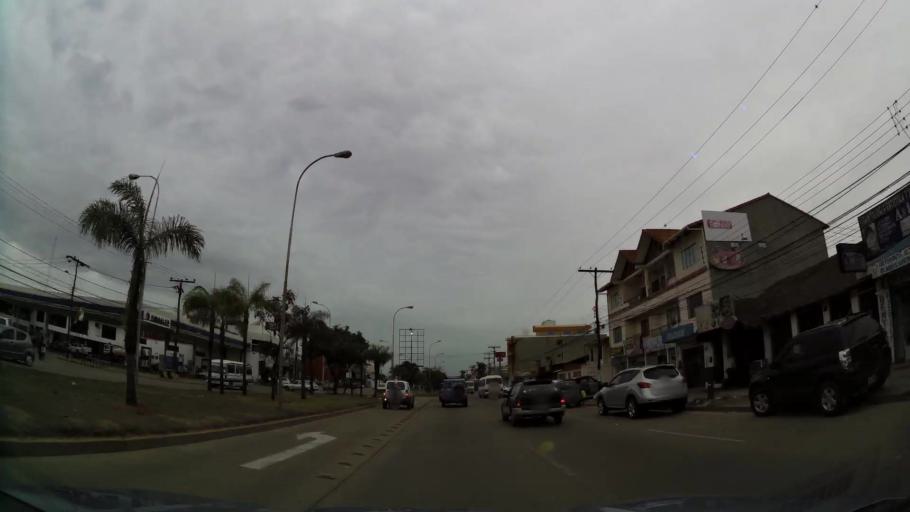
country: BO
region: Santa Cruz
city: Santa Cruz de la Sierra
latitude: -17.8159
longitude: -63.1834
